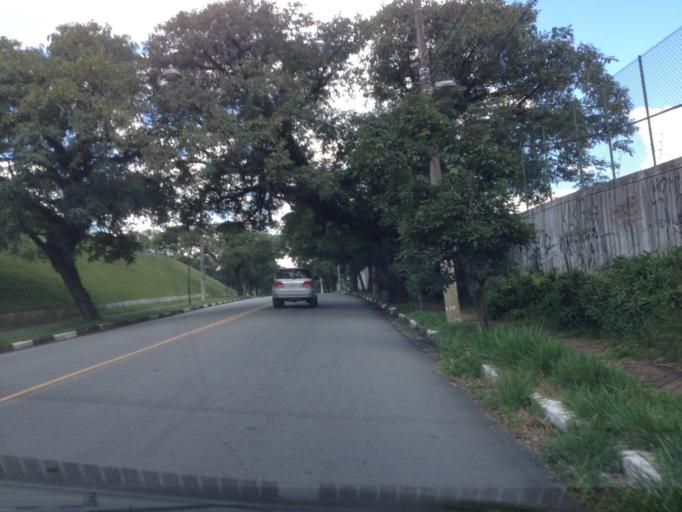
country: BR
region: Sao Paulo
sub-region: Sao Paulo
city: Sao Paulo
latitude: -23.5533
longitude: -46.7046
